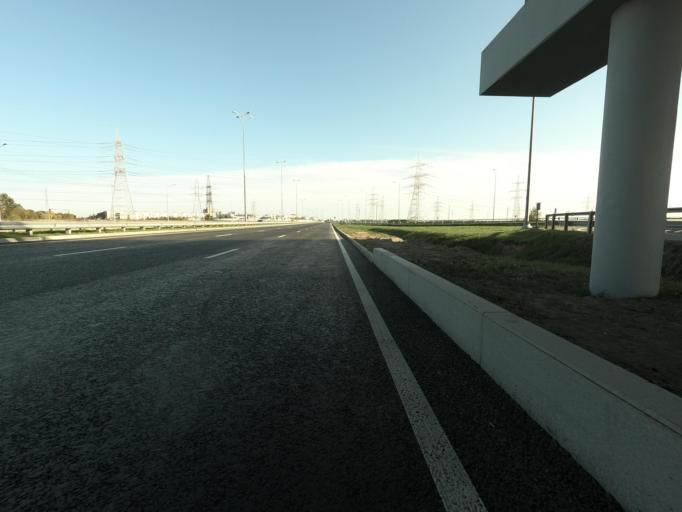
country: RU
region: St.-Petersburg
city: Kolpino
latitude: 59.7432
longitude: 30.5415
